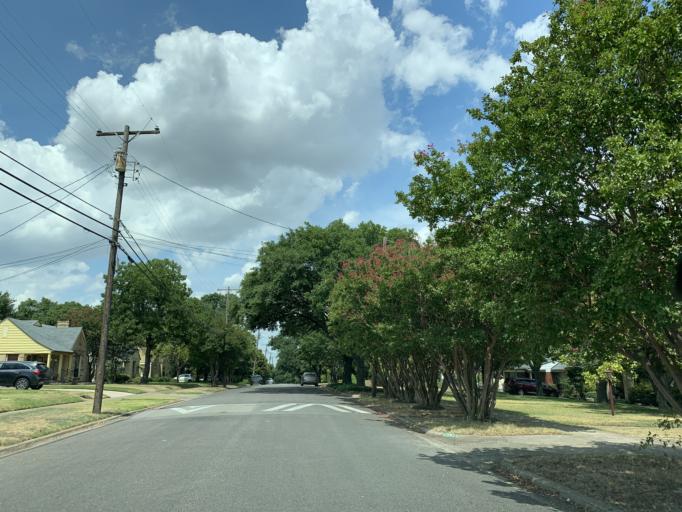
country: US
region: Texas
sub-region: Dallas County
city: Cockrell Hill
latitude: 32.7503
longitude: -96.8546
